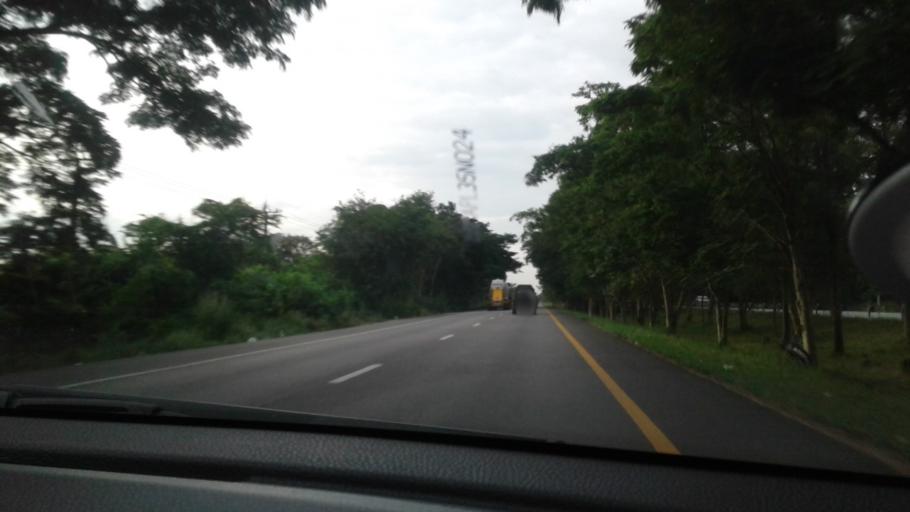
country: TH
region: Prachuap Khiri Khan
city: Pran Buri
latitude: 12.4389
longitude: 99.9106
